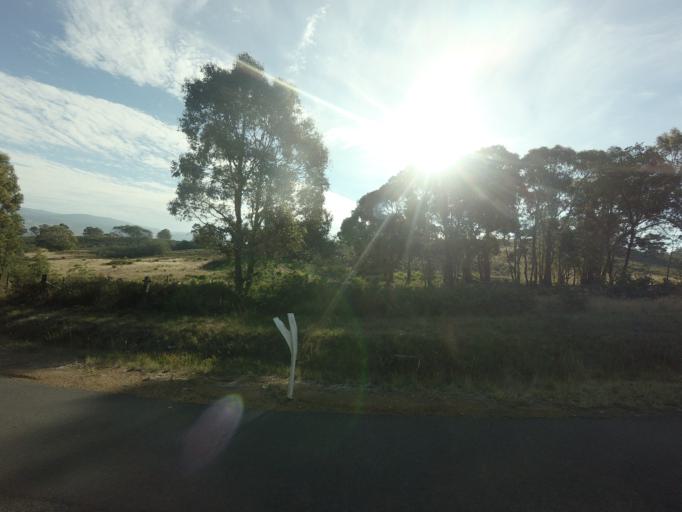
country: AU
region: Tasmania
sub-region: Brighton
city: Bridgewater
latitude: -42.5173
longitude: 147.3847
